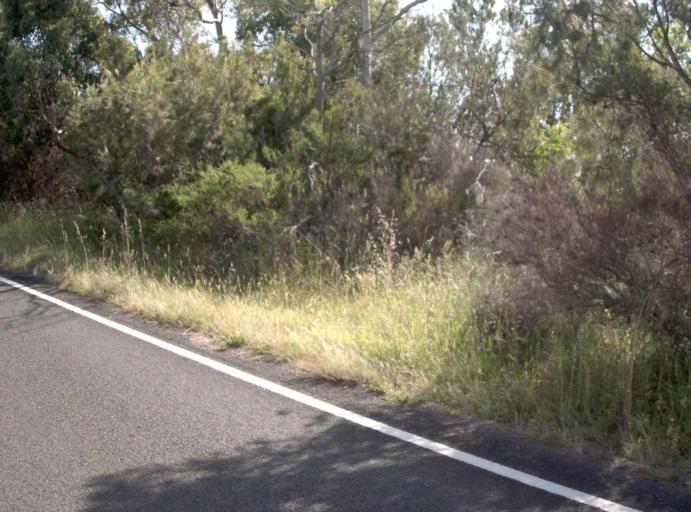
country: AU
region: Victoria
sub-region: Cardinia
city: Koo-Wee-Rup
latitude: -38.3105
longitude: 145.5416
